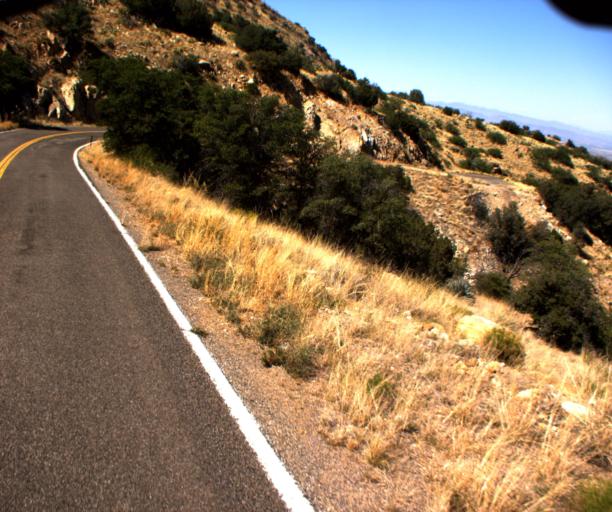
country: US
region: Arizona
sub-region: Graham County
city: Swift Trail Junction
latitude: 32.6711
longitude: -109.7861
